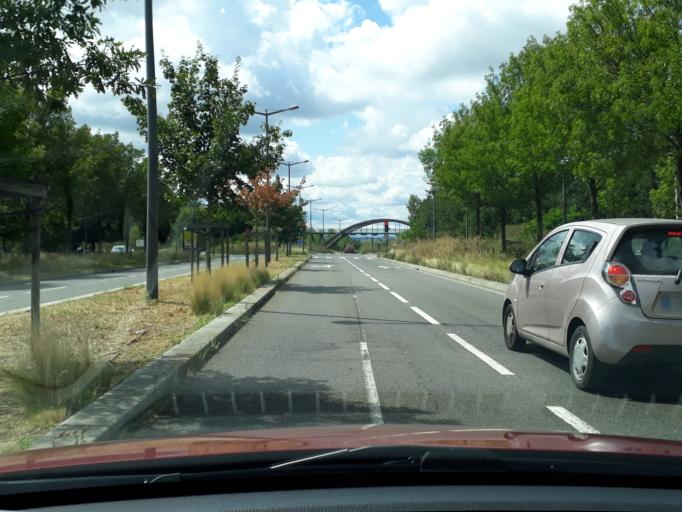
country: FR
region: Rhone-Alpes
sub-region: Departement du Rhone
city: Bron
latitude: 45.7155
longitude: 4.9262
